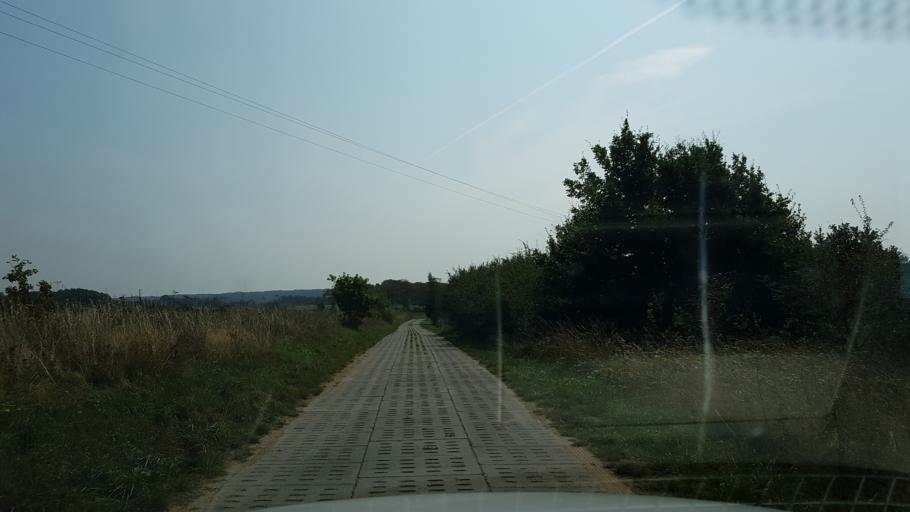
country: PL
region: West Pomeranian Voivodeship
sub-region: Powiat slawienski
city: Darlowo
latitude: 54.5045
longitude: 16.5027
